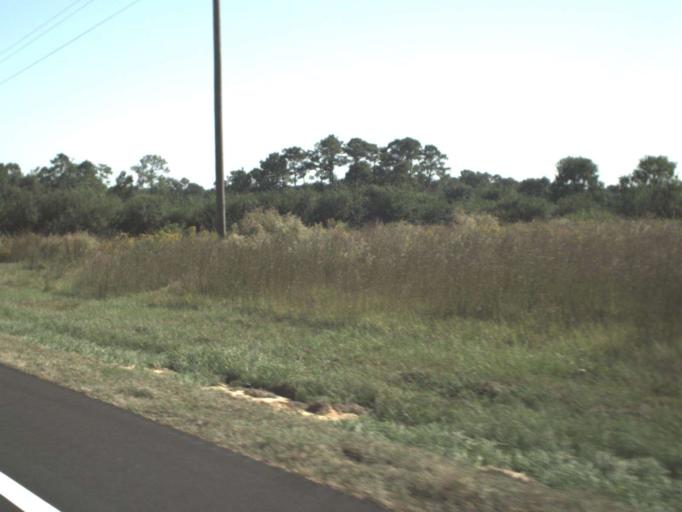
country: US
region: Alabama
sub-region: Covington County
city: Florala
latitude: 30.8757
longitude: -86.2631
